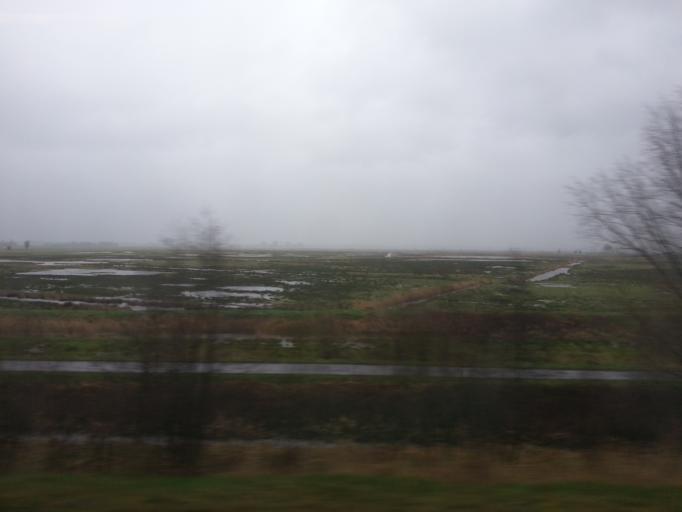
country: NL
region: North Brabant
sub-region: Gemeente Breda
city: Breda
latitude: 51.6343
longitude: 4.7018
